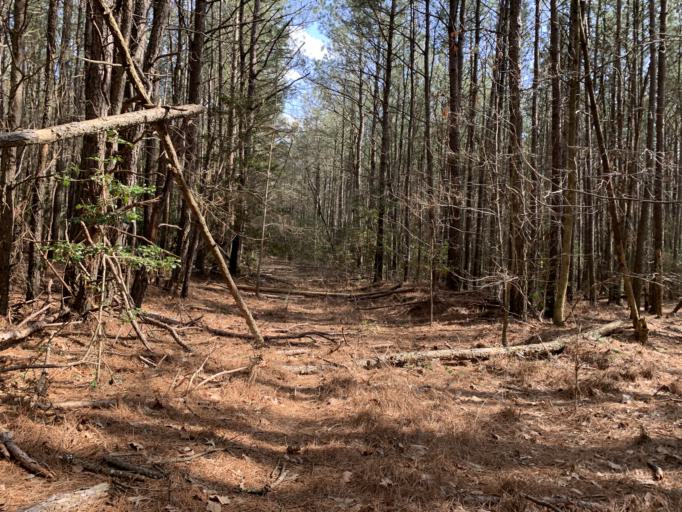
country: US
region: Delaware
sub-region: Sussex County
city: Georgetown
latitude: 38.6784
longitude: -75.4761
